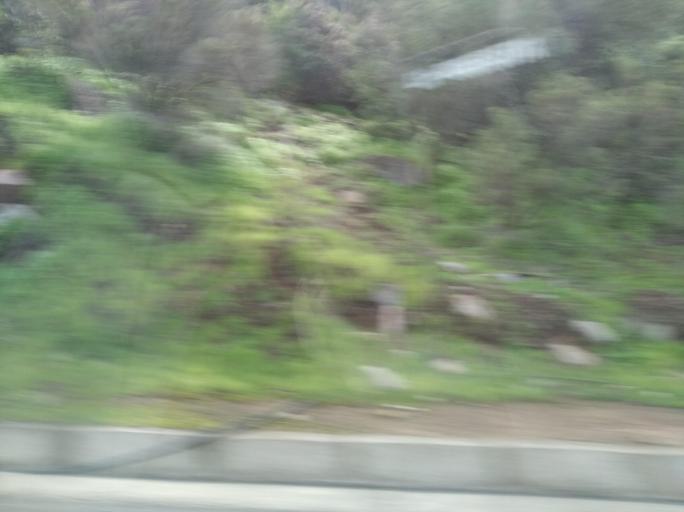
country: CL
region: Valparaiso
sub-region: Provincia de San Felipe
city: Llaillay
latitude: -33.0705
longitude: -70.9747
